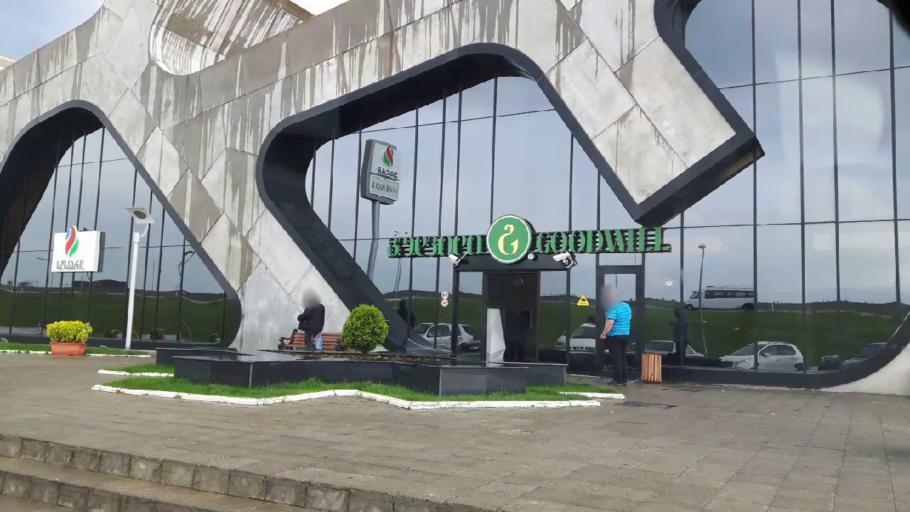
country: GE
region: Shida Kartli
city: Gori
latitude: 42.0167
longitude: 44.0258
